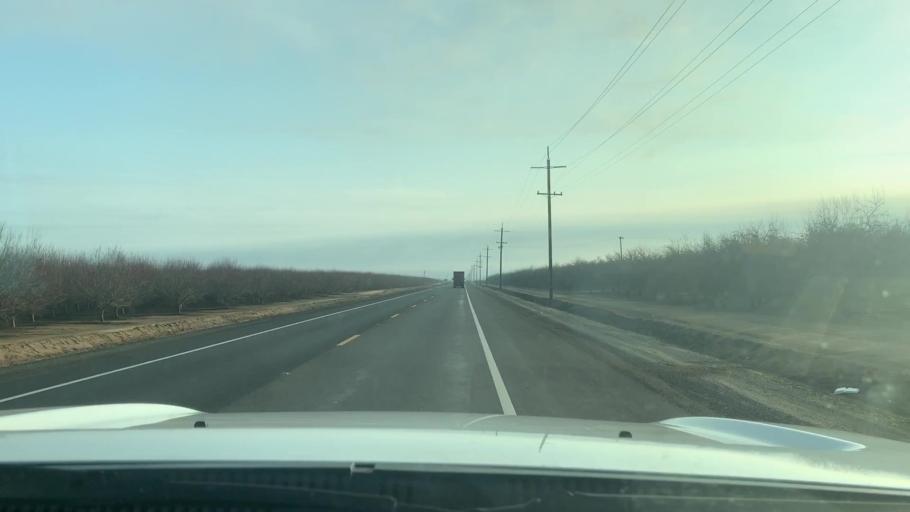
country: US
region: California
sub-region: Kern County
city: McFarland
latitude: 35.6019
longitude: -119.2476
